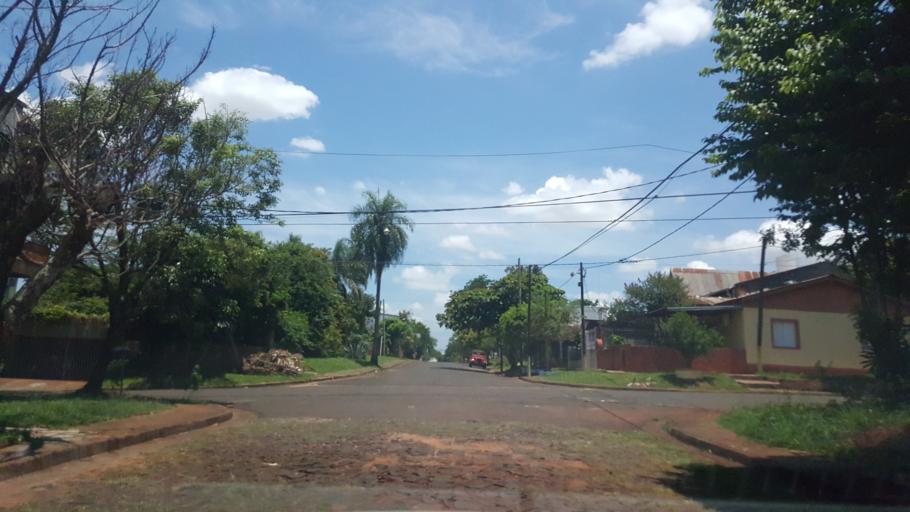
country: AR
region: Misiones
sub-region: Departamento de Capital
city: Posadas
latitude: -27.3846
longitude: -55.9081
